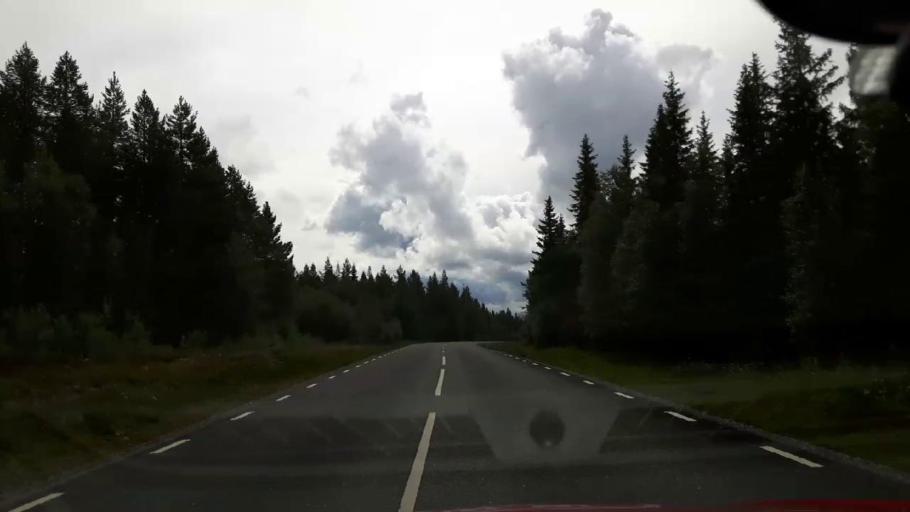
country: NO
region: Nord-Trondelag
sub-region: Lierne
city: Sandvika
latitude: 64.6237
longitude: 14.1223
